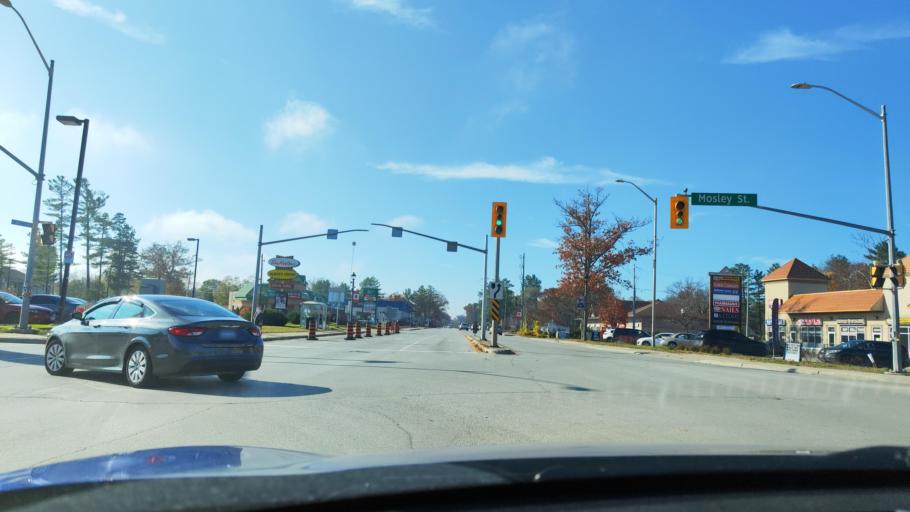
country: CA
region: Ontario
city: Wasaga Beach
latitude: 44.4895
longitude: -80.0509
